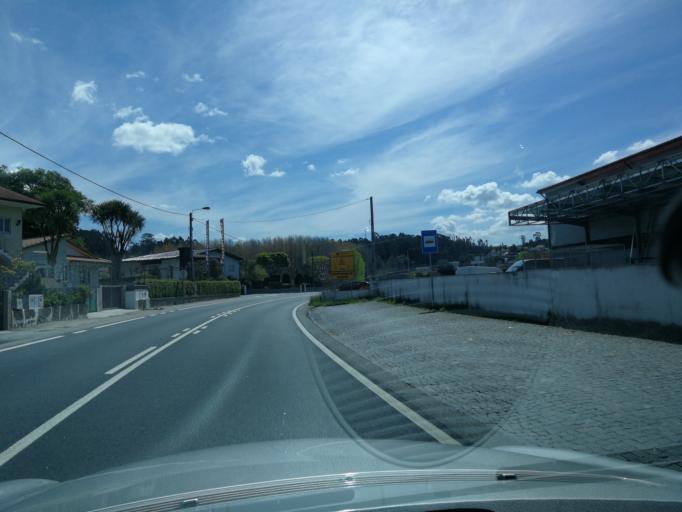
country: PT
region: Braga
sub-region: Vila Nova de Famalicao
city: Calendario
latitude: 41.4290
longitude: -8.5350
